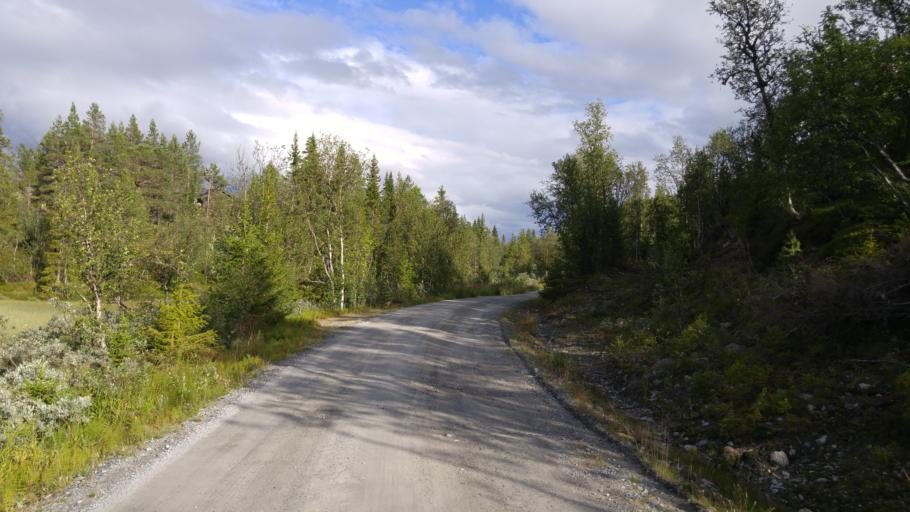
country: NO
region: Buskerud
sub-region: Hemsedal
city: Troim
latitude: 60.8492
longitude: 8.7111
